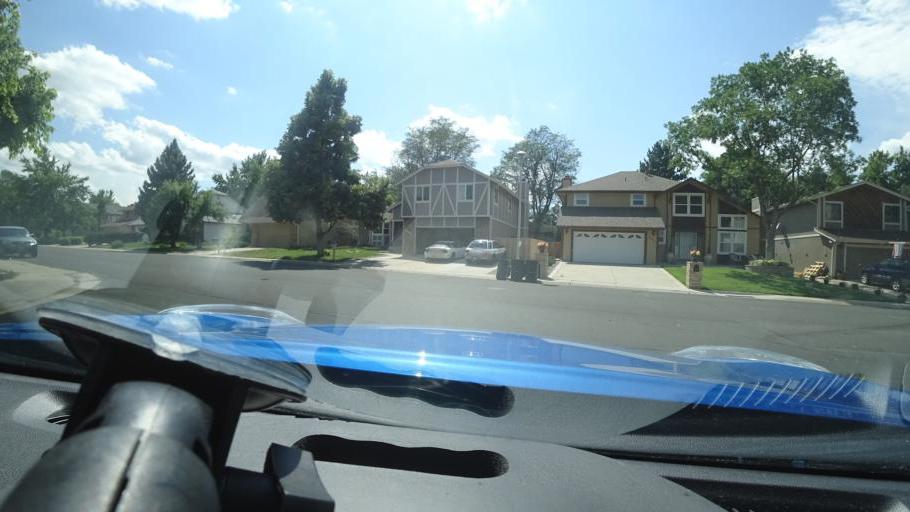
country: US
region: Colorado
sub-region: Adams County
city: Aurora
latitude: 39.6780
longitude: -104.8536
